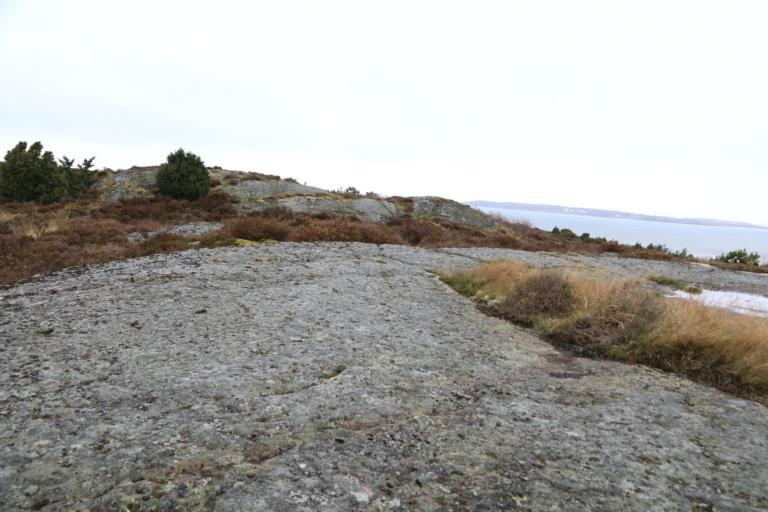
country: SE
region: Halland
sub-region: Kungsbacka Kommun
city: Frillesas
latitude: 57.3046
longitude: 12.1717
